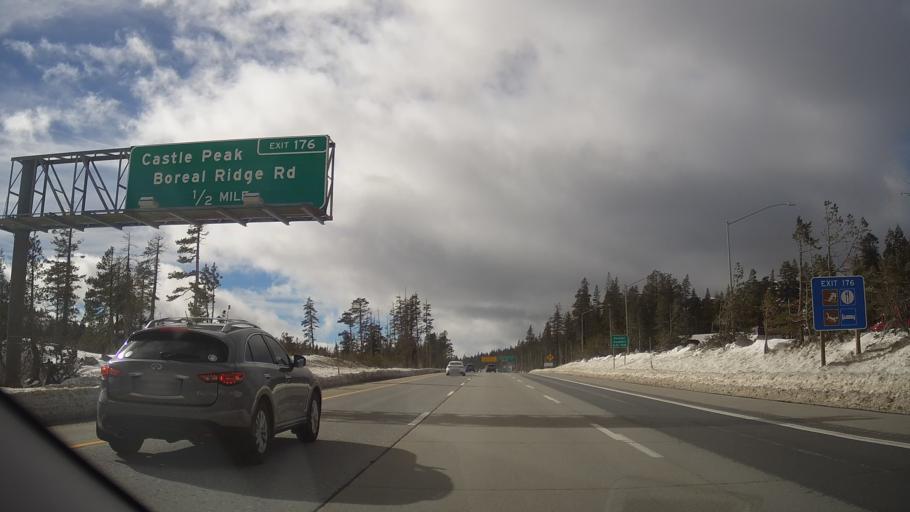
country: US
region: California
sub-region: Nevada County
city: Truckee
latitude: 39.3424
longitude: -120.3393
